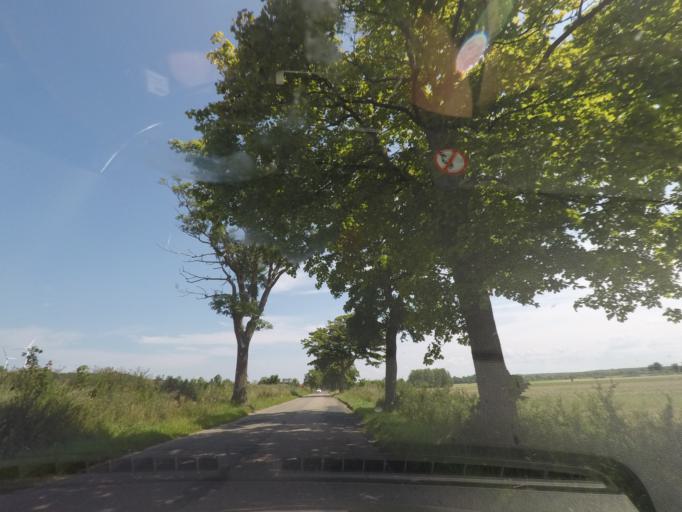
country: PL
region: West Pomeranian Voivodeship
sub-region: Powiat slawienski
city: Darlowo
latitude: 54.4611
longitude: 16.5162
